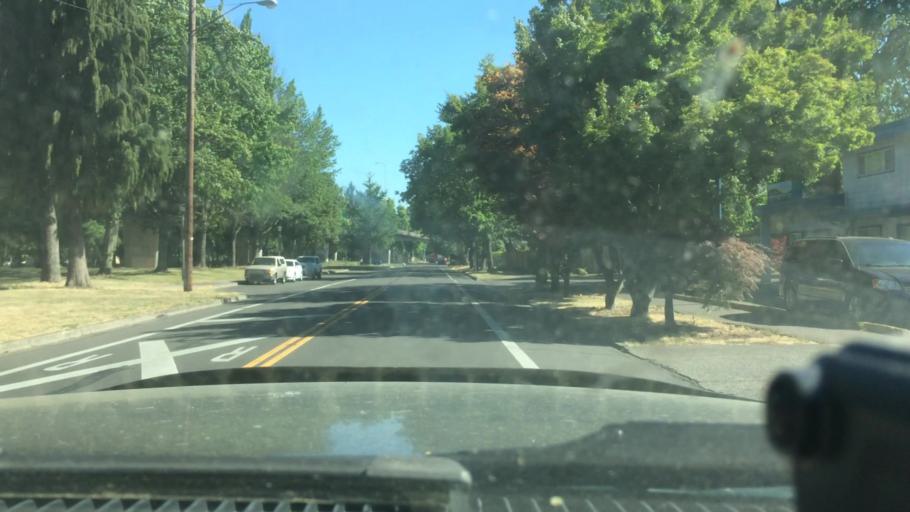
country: US
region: Oregon
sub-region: Lane County
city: Eugene
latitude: 44.0559
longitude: -123.1019
